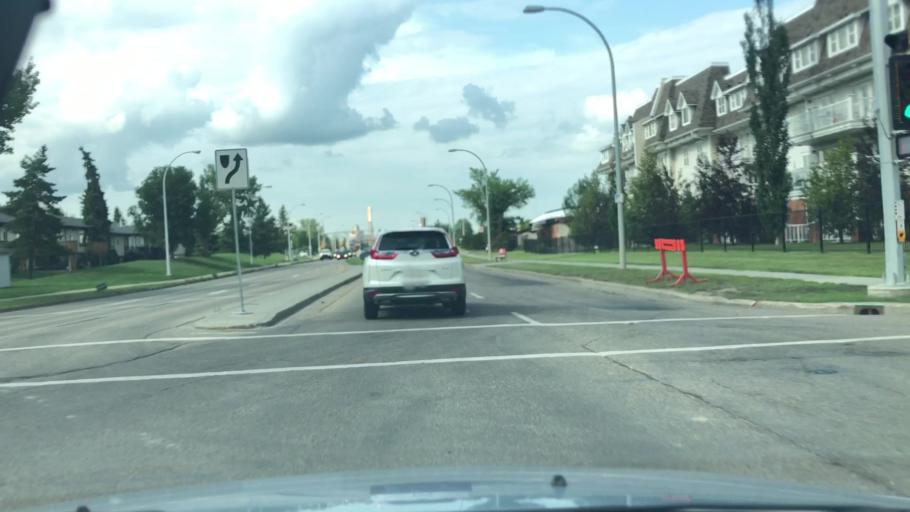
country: CA
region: Alberta
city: Edmonton
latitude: 53.6119
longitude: -113.5167
